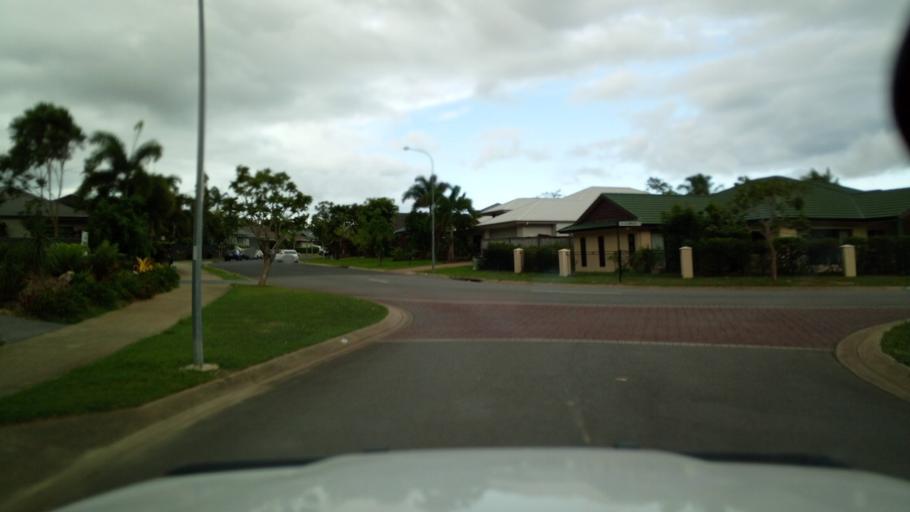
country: AU
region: Queensland
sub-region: Cairns
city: Redlynch
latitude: -16.8426
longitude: 145.6887
